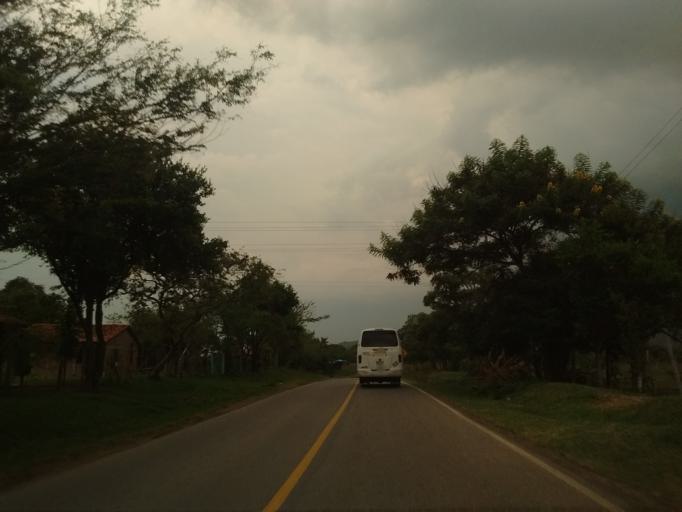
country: CO
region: Cauca
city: Caloto
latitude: 3.0620
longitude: -76.3678
